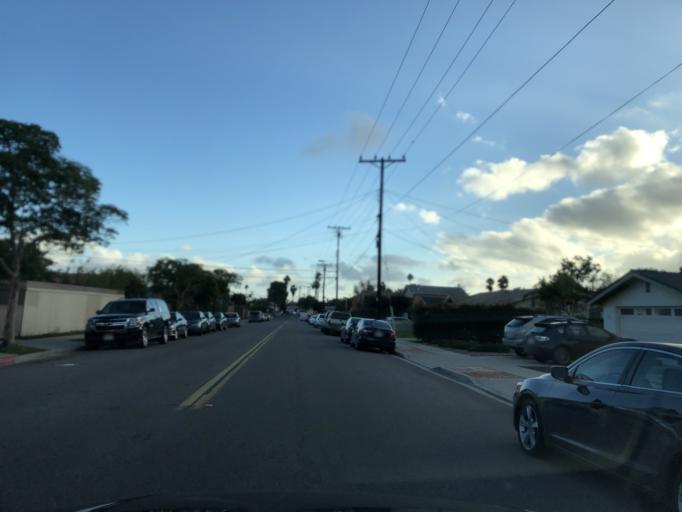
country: US
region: California
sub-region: San Diego County
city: La Jolla
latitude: 32.8187
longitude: -117.1754
